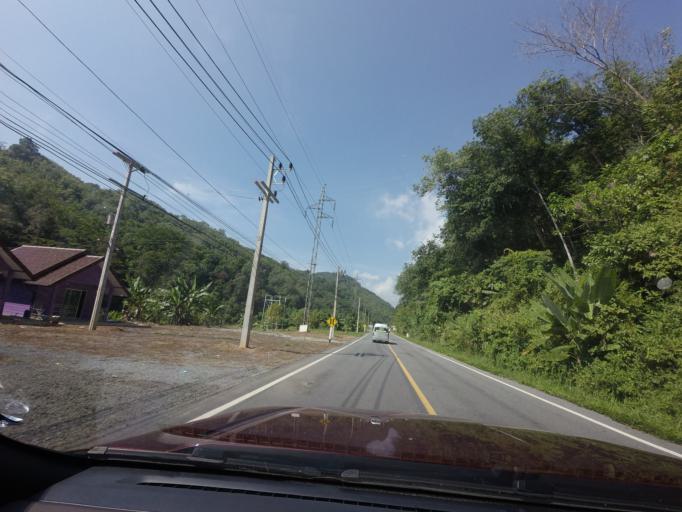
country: TH
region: Yala
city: Betong
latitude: 5.9451
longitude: 101.1900
